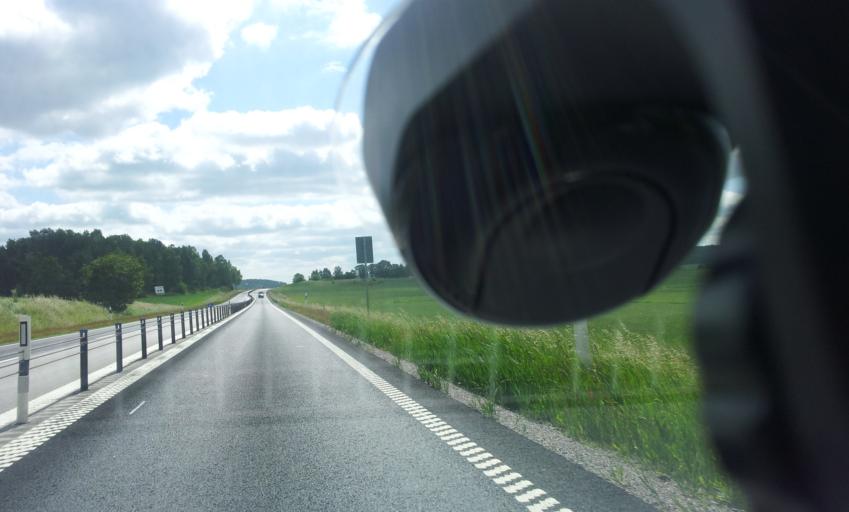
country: SE
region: OEstergoetland
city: Lindo
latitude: 58.5489
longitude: 16.2566
